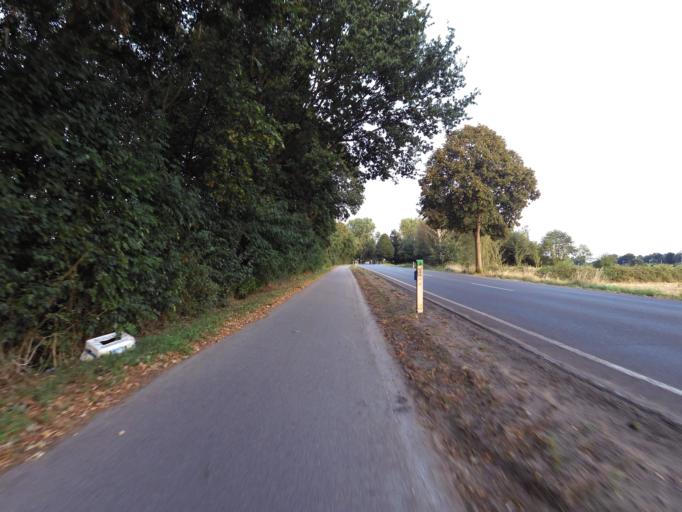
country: DE
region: North Rhine-Westphalia
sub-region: Regierungsbezirk Dusseldorf
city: Emmerich
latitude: 51.8615
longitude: 6.1824
